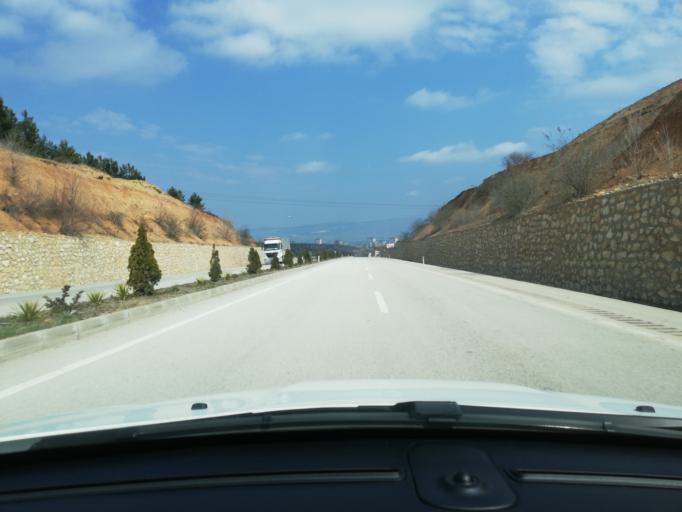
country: TR
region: Kastamonu
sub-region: Cide
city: Kastamonu
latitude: 41.3844
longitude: 33.8084
